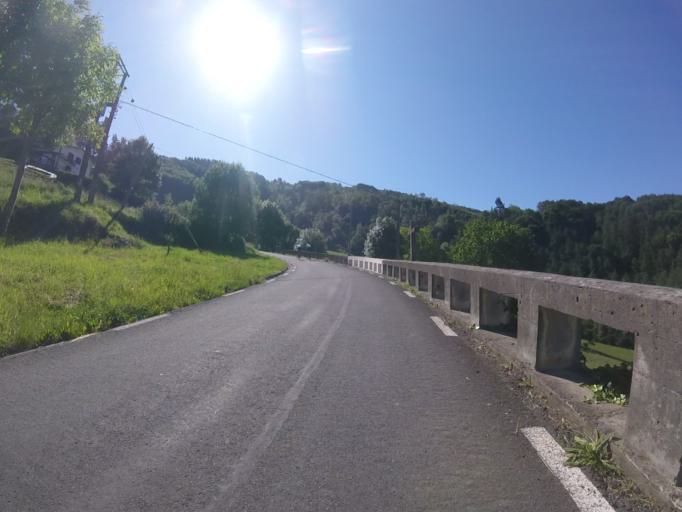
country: ES
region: Basque Country
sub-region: Provincia de Guipuzcoa
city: Beizama
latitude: 43.1331
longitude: -2.1982
